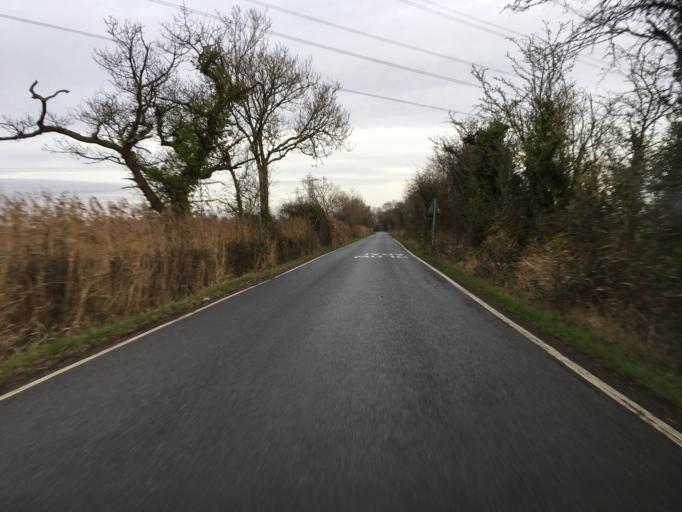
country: GB
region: Wales
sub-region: Newport
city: Bishton
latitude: 51.5595
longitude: -2.8916
